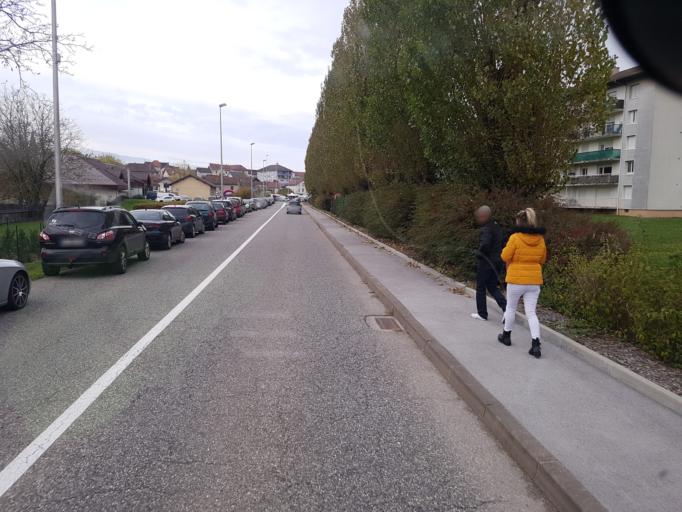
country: FR
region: Rhone-Alpes
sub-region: Departement de la Haute-Savoie
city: Versonnex
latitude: 45.9556
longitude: 5.8373
